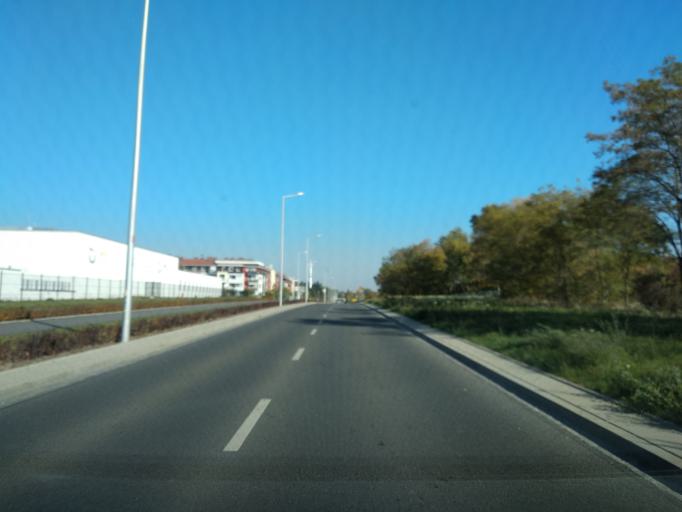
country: PL
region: Lower Silesian Voivodeship
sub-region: Powiat wroclawski
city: Bielany Wroclawskie
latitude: 51.0788
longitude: 16.9899
